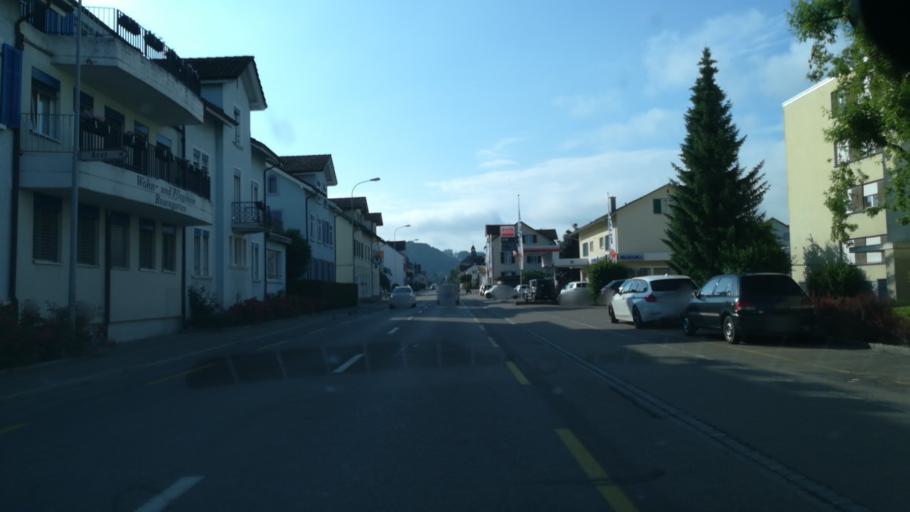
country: CH
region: Thurgau
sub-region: Weinfelden District
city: Sulgen
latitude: 47.5281
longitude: 9.1951
